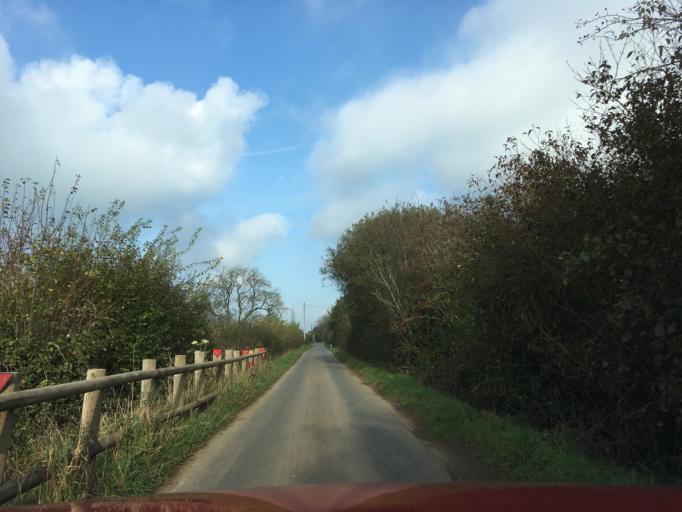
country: GB
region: England
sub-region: South Gloucestershire
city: Yate
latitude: 51.5686
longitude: -2.4251
